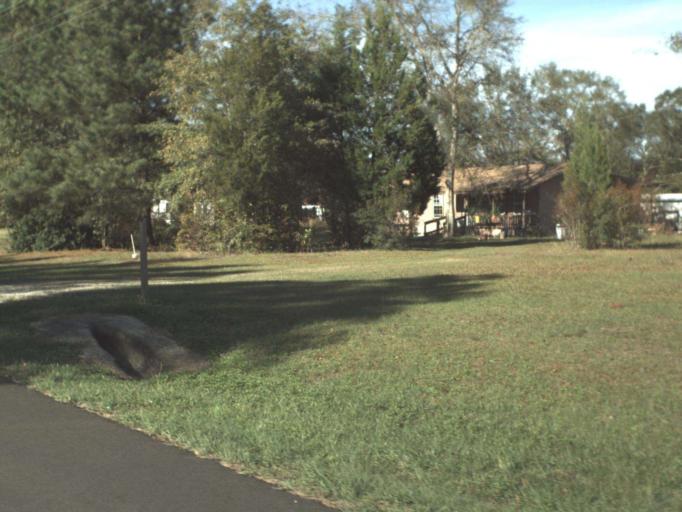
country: US
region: Alabama
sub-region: Escambia County
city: East Brewton
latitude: 30.8943
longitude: -86.9854
